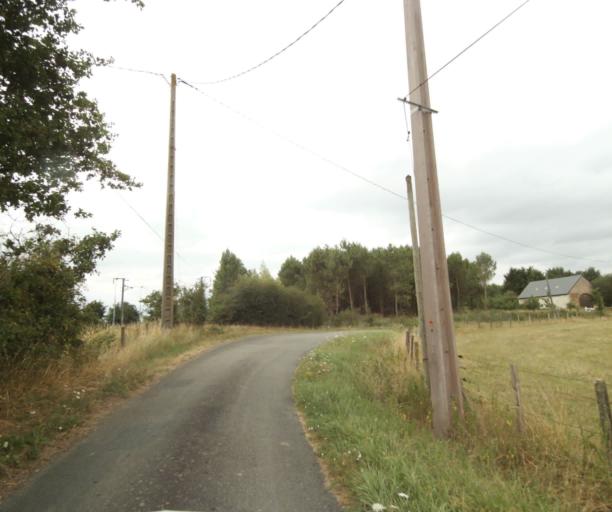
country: FR
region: Pays de la Loire
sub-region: Departement de la Sarthe
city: Sable-sur-Sarthe
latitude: 47.8072
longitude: -0.3772
